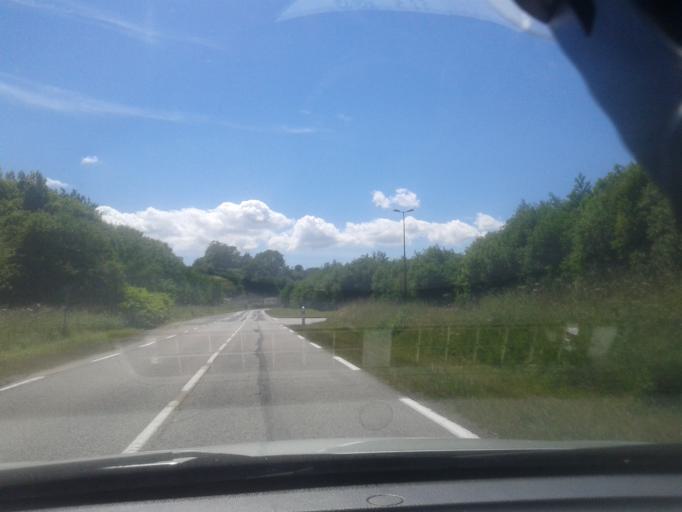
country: FR
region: Lower Normandy
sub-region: Departement de la Manche
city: Octeville
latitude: 49.6163
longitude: -1.6376
